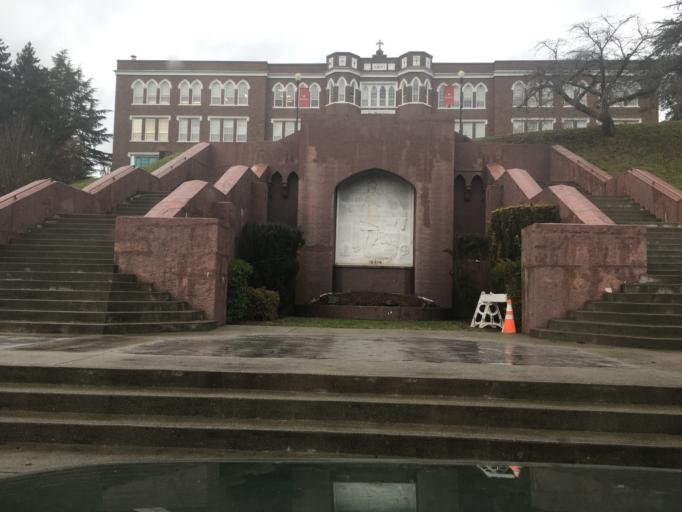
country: US
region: Washington
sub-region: Thurston County
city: Lacey
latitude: 47.0395
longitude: -122.8152
